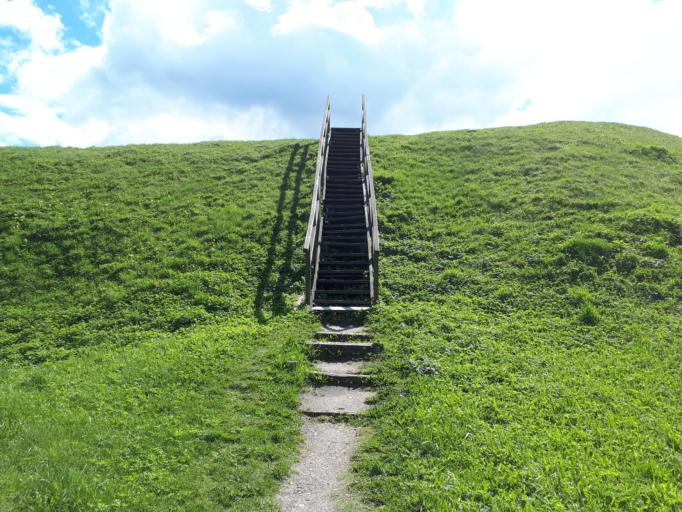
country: LT
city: Simnas
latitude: 54.3128
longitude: 23.6547
